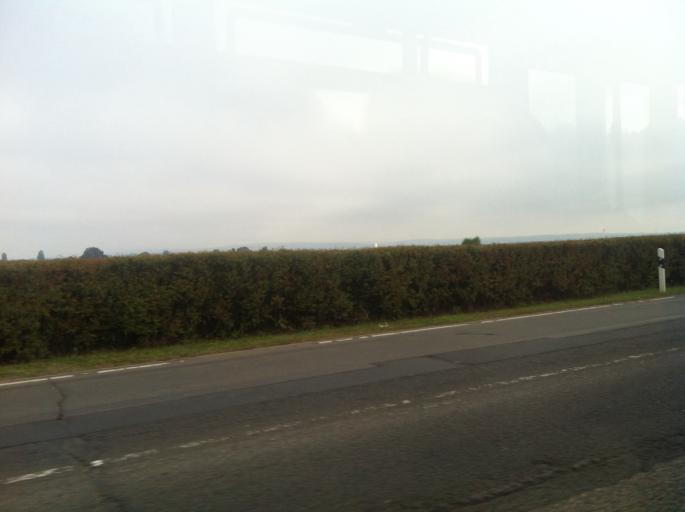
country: DE
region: Hesse
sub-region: Regierungsbezirk Darmstadt
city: Hochheim am Main
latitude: 50.0445
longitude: 8.3072
